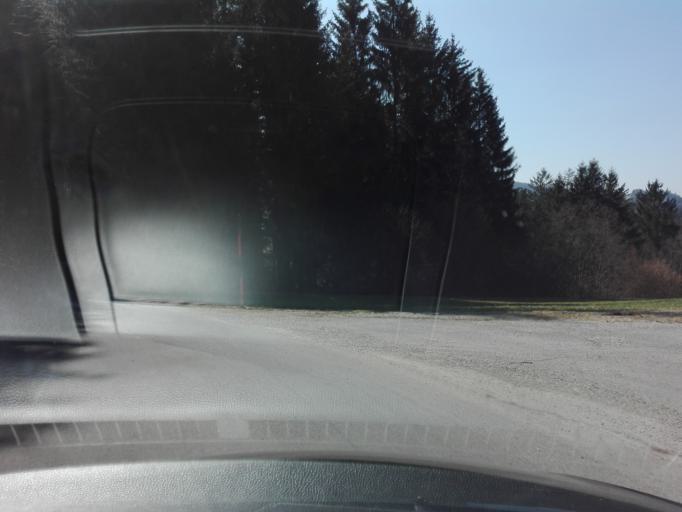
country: AT
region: Upper Austria
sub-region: Politischer Bezirk Perg
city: Bad Kreuzen
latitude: 48.3495
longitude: 14.7239
